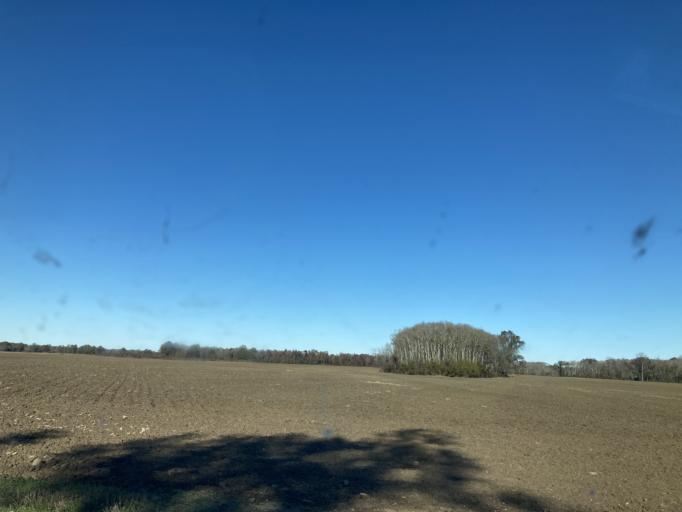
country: US
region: Mississippi
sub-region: Yazoo County
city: Yazoo City
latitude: 32.7386
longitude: -90.6324
